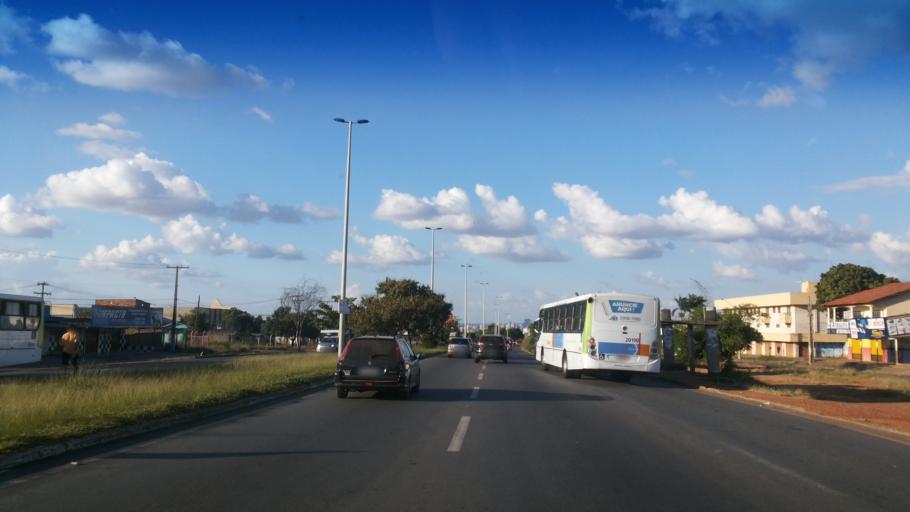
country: BR
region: Goias
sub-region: Goiania
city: Goiania
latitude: -16.7517
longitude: -49.3350
